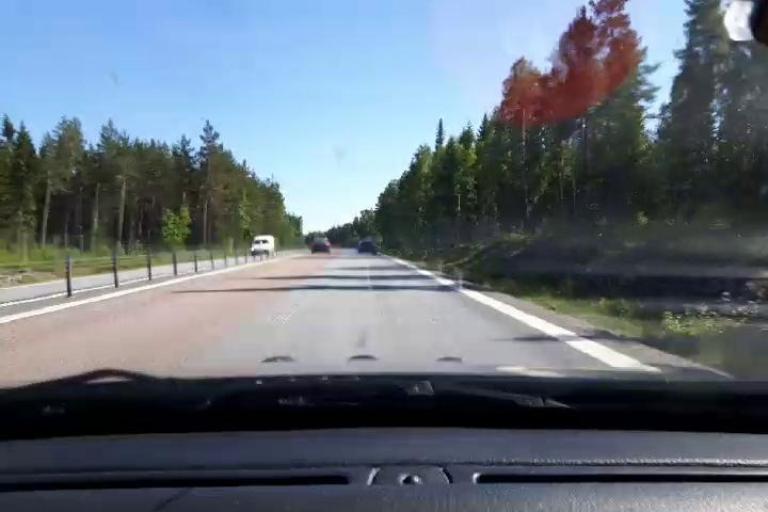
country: SE
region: Gaevleborg
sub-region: Gavle Kommun
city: Norrsundet
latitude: 60.8781
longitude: 17.0468
